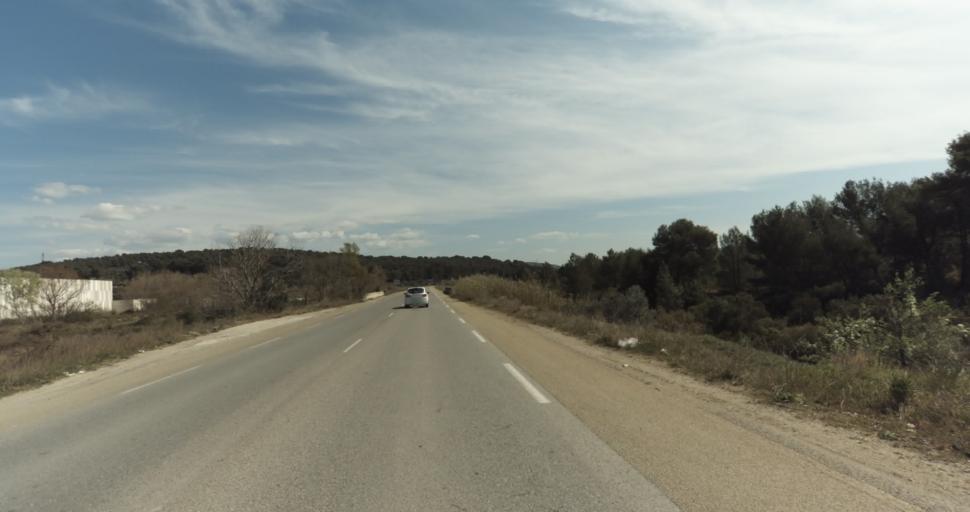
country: FR
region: Provence-Alpes-Cote d'Azur
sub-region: Departement des Bouches-du-Rhone
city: Coudoux
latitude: 43.5466
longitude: 5.2525
